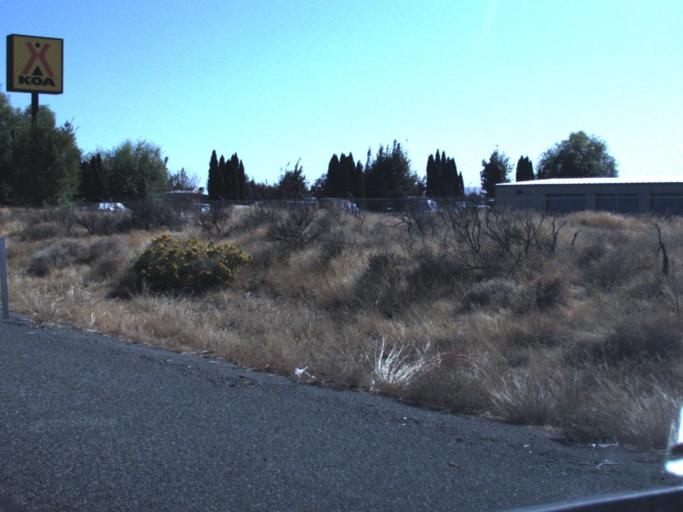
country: US
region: Washington
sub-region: Franklin County
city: West Pasco
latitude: 46.2727
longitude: -119.2058
